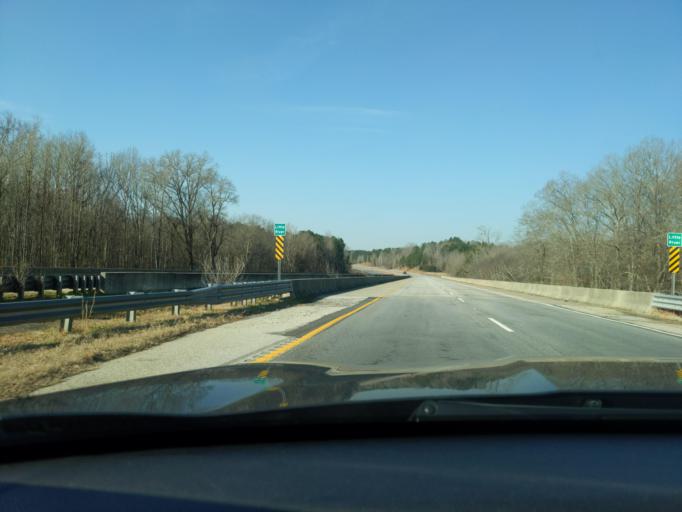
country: US
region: South Carolina
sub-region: Abbeville County
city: Calhoun Falls
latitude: 34.1107
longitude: -82.5095
